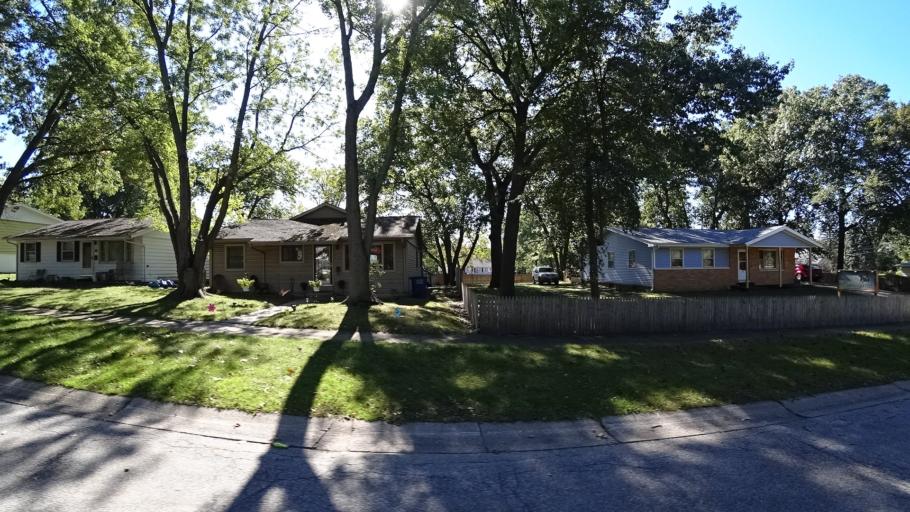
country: US
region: Indiana
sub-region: LaPorte County
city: Michigan City
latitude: 41.7099
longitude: -86.9185
